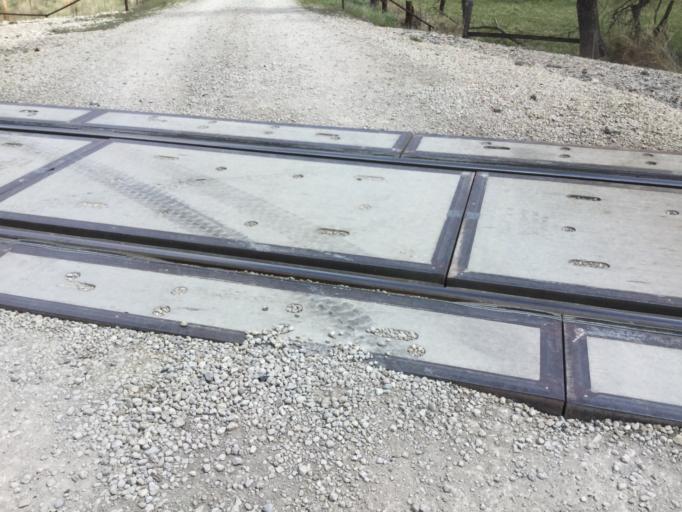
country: US
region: Kansas
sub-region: Crawford County
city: Arma
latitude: 37.6881
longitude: -94.6278
